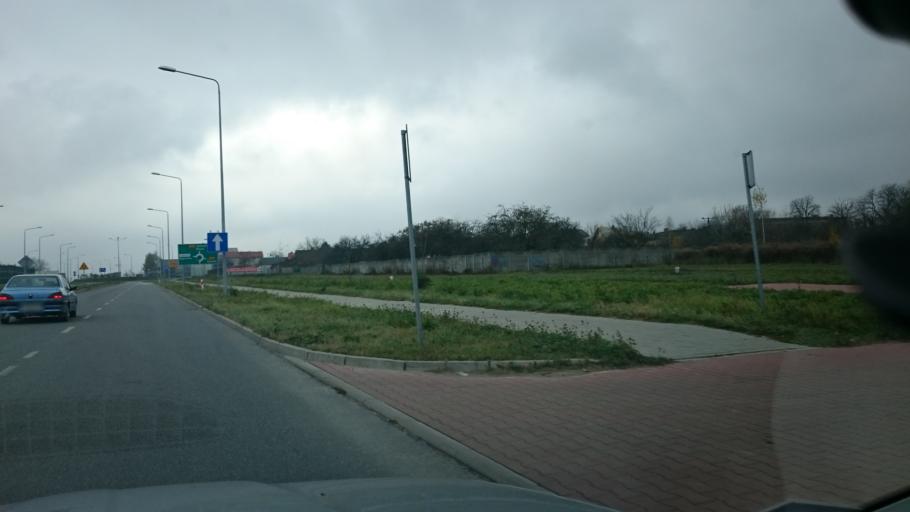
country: PL
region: Swietokrzyskie
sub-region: Powiat konecki
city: Konskie
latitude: 51.1954
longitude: 20.3993
